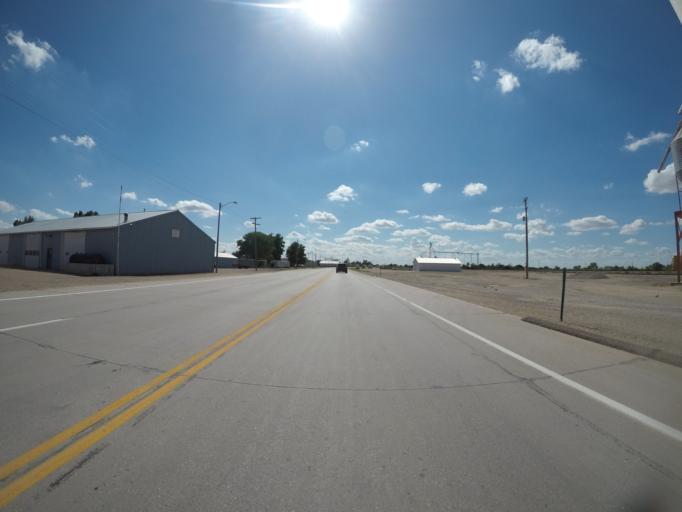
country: US
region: Colorado
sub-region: Phillips County
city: Holyoke
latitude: 40.5855
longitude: -102.3066
